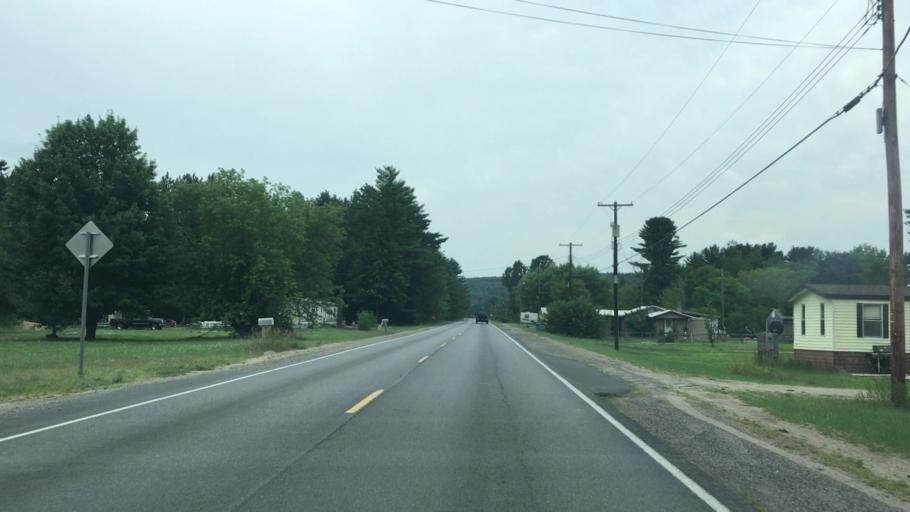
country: US
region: New York
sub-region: Clinton County
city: Peru
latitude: 44.5234
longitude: -73.5729
